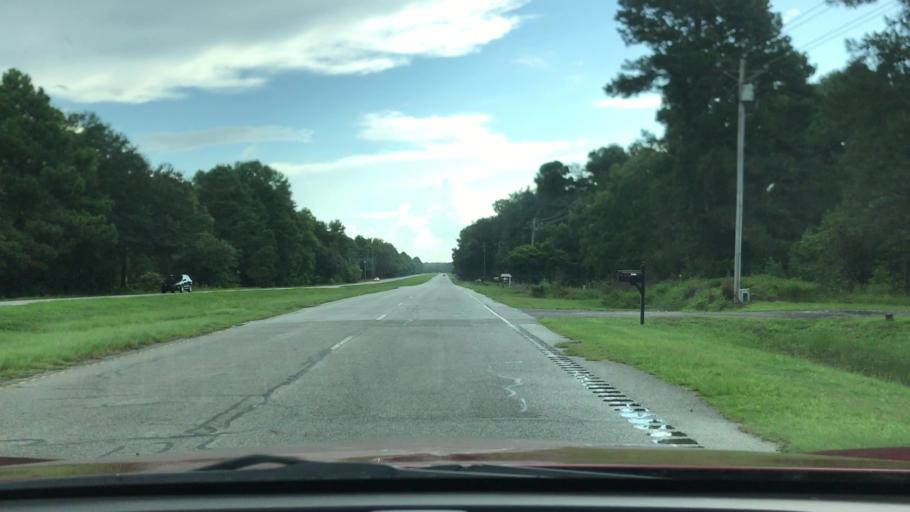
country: US
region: South Carolina
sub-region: Charleston County
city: Awendaw
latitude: 33.0494
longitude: -79.5596
